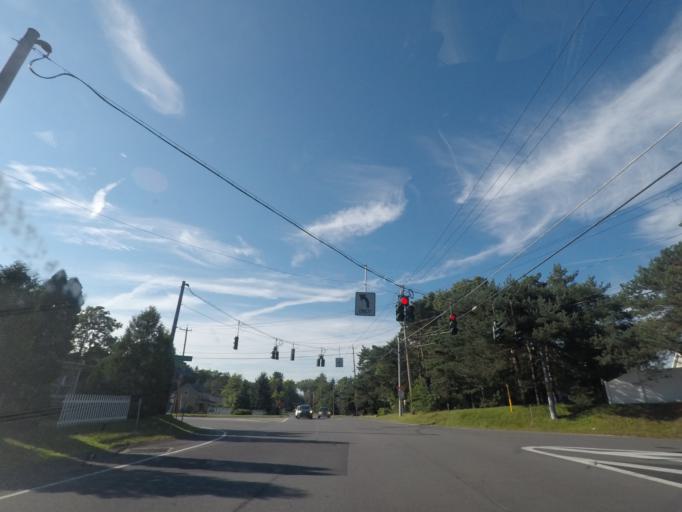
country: US
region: New York
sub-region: Albany County
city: West Albany
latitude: 42.7272
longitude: -73.7740
